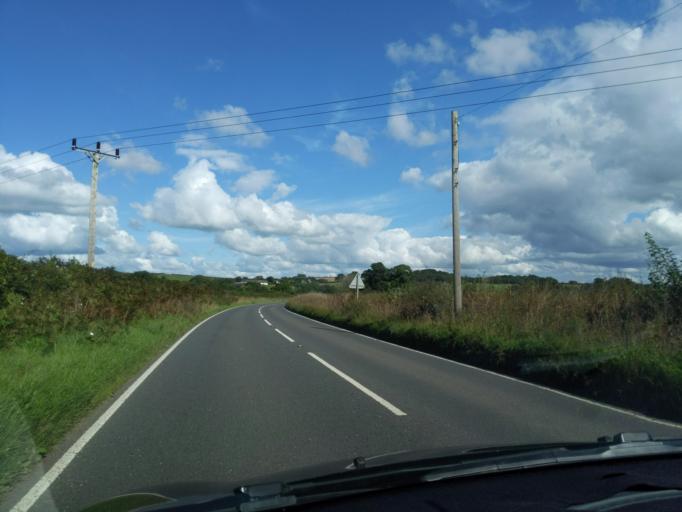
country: GB
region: England
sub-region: Cornwall
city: Launceston
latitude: 50.6544
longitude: -4.3431
